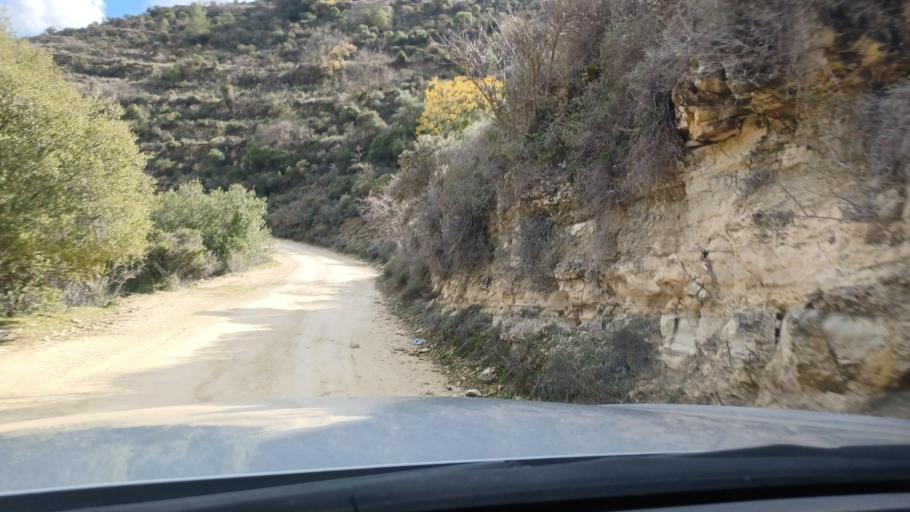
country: CY
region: Limassol
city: Pachna
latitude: 34.8317
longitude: 32.7643
